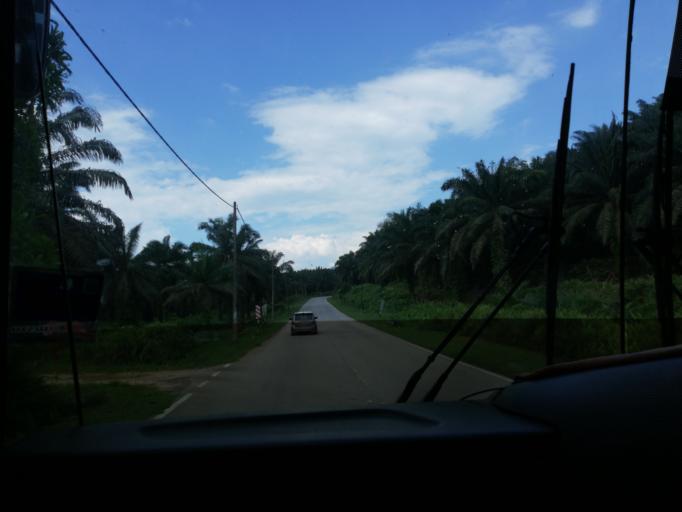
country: MY
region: Kedah
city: Kulim
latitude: 5.2653
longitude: 100.6081
